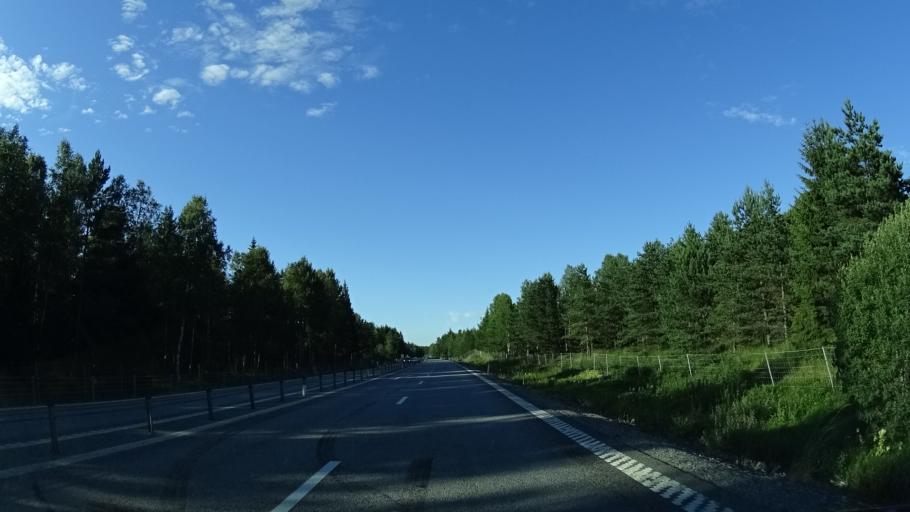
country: SE
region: Stockholm
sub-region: Osterakers Kommun
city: Akersberga
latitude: 59.6000
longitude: 18.2742
